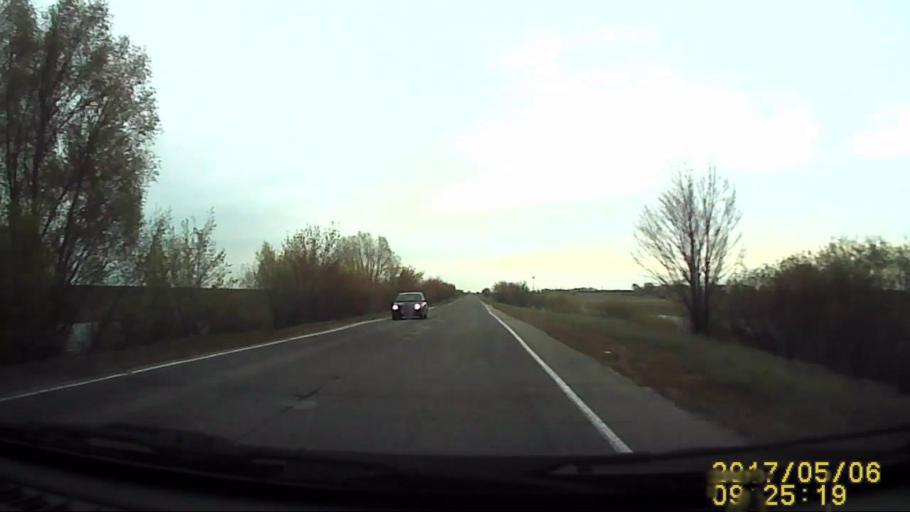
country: RU
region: Ulyanovsk
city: Cherdakly
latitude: 54.3824
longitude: 48.8199
